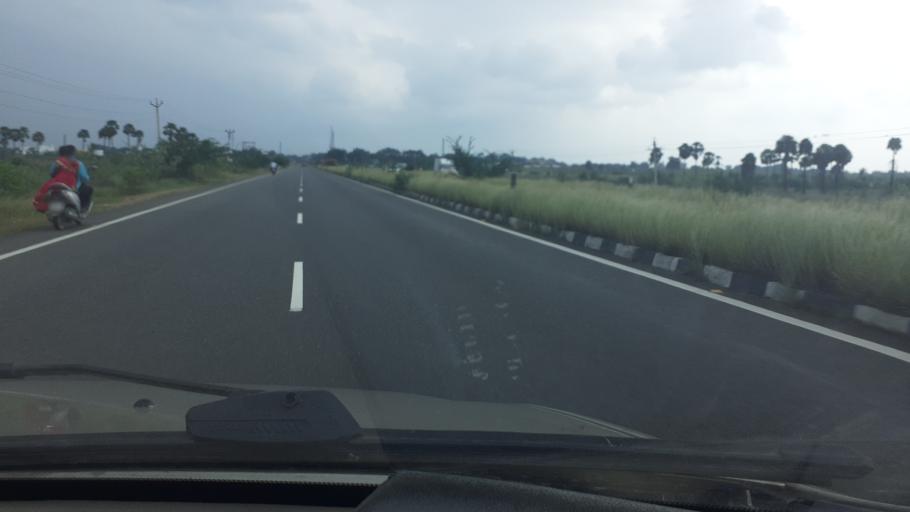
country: IN
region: Tamil Nadu
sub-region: Madurai
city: Kallupatti
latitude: 9.7077
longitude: 77.9743
